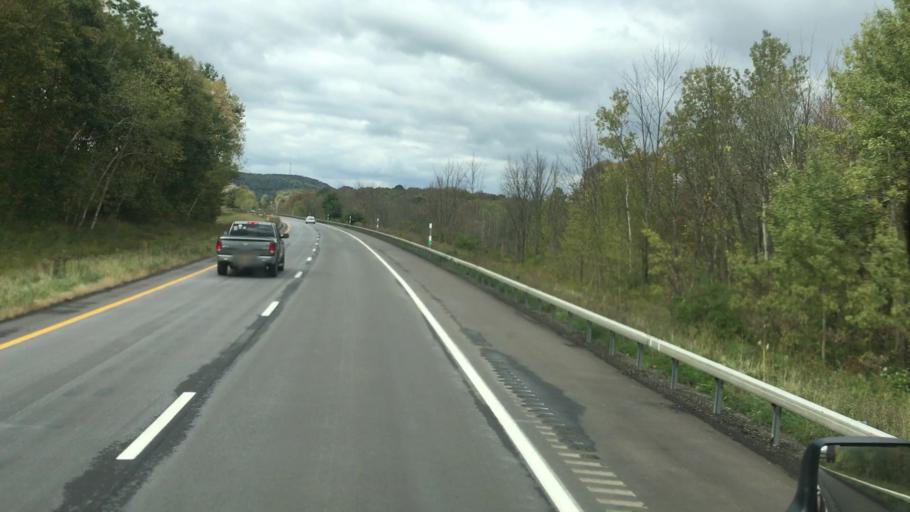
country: US
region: New York
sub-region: Cattaraugus County
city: Randolph
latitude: 42.1166
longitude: -78.9266
